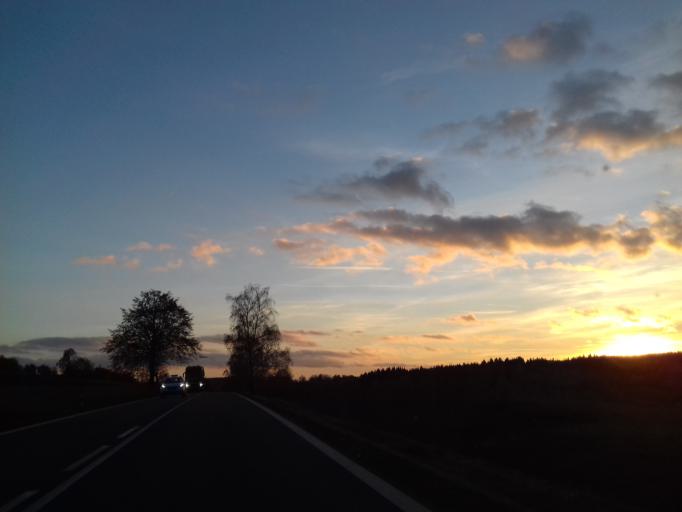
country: CZ
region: Vysocina
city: Krizova
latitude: 49.7241
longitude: 15.8662
